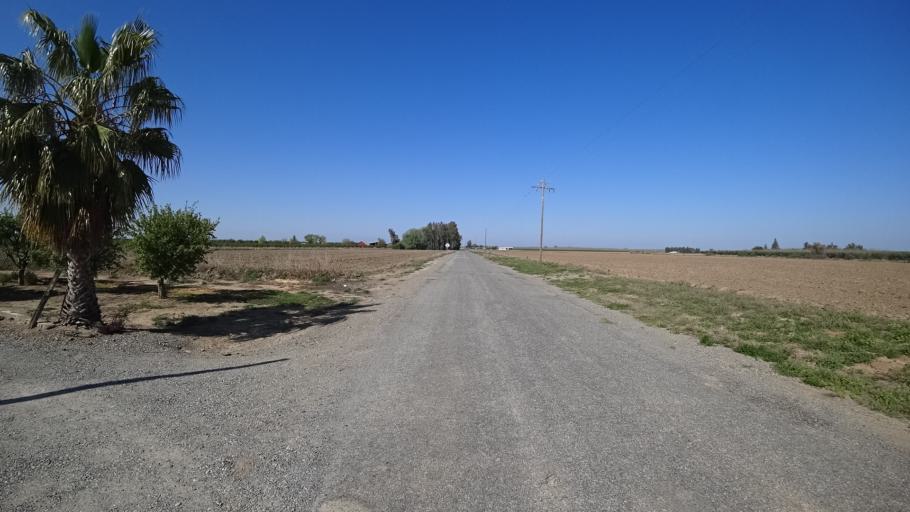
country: US
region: California
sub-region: Glenn County
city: Hamilton City
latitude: 39.6523
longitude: -122.0089
